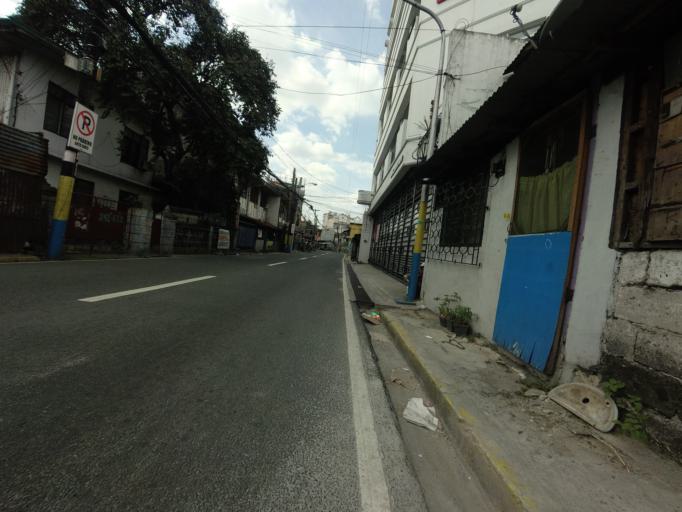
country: PH
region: Metro Manila
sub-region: San Juan
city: San Juan
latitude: 14.5890
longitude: 121.0310
